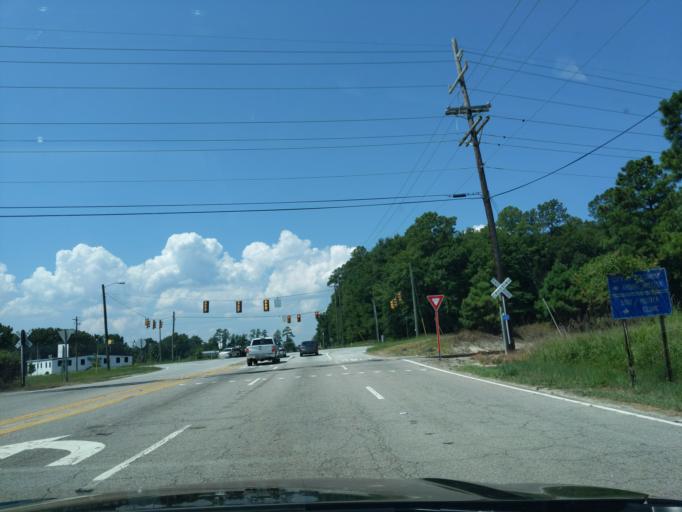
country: US
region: South Carolina
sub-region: Richland County
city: Forest Acres
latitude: 33.9590
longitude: -80.9839
